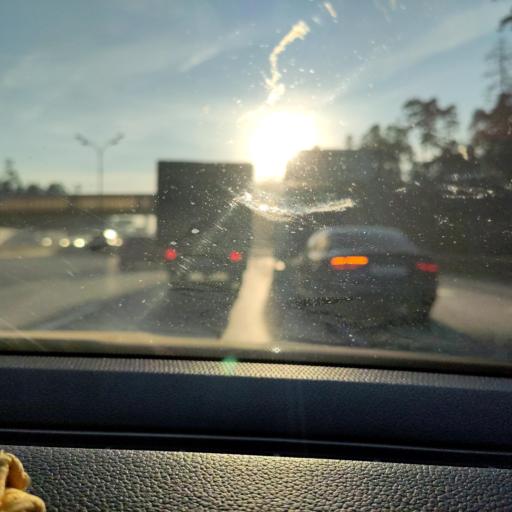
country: RU
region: Moscow
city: Rublevo
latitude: 55.7865
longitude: 37.3704
